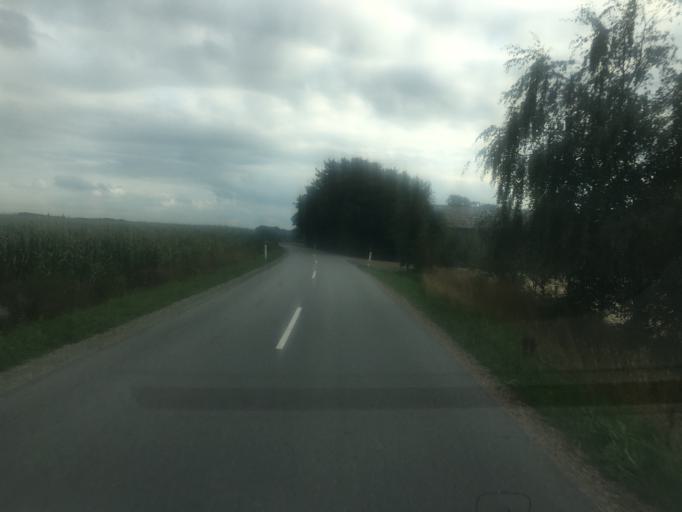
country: DK
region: South Denmark
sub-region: Tonder Kommune
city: Logumkloster
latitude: 54.9766
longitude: 8.9534
